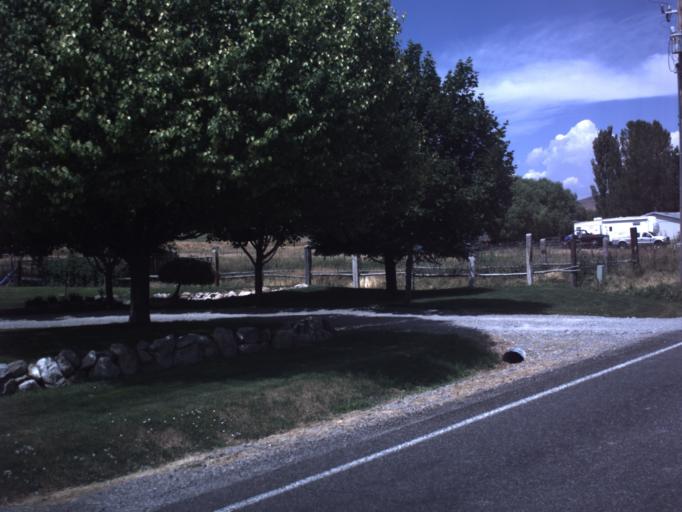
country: US
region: Utah
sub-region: Box Elder County
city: Tremonton
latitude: 41.6750
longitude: -112.2967
